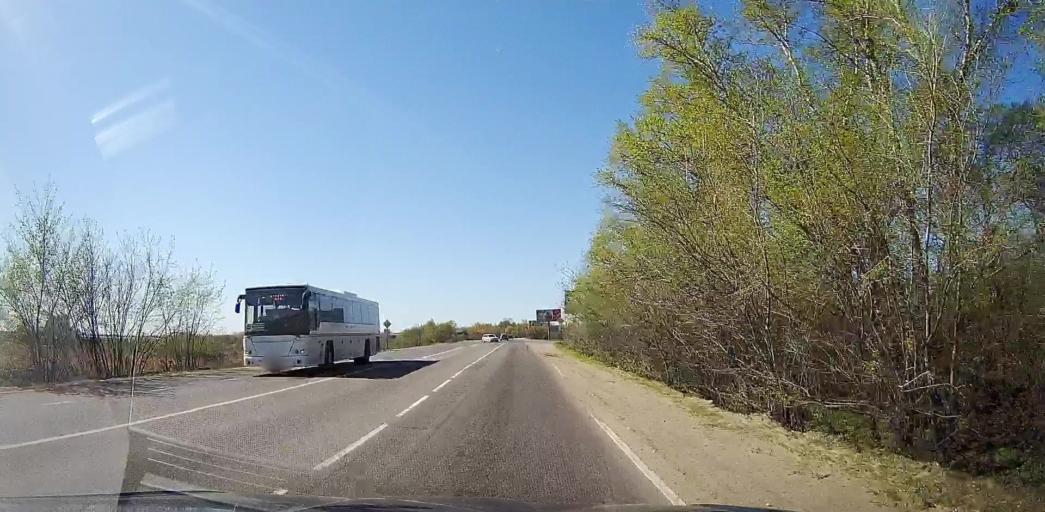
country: RU
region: Moskovskaya
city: Ramenskoye
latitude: 55.5444
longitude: 38.2822
